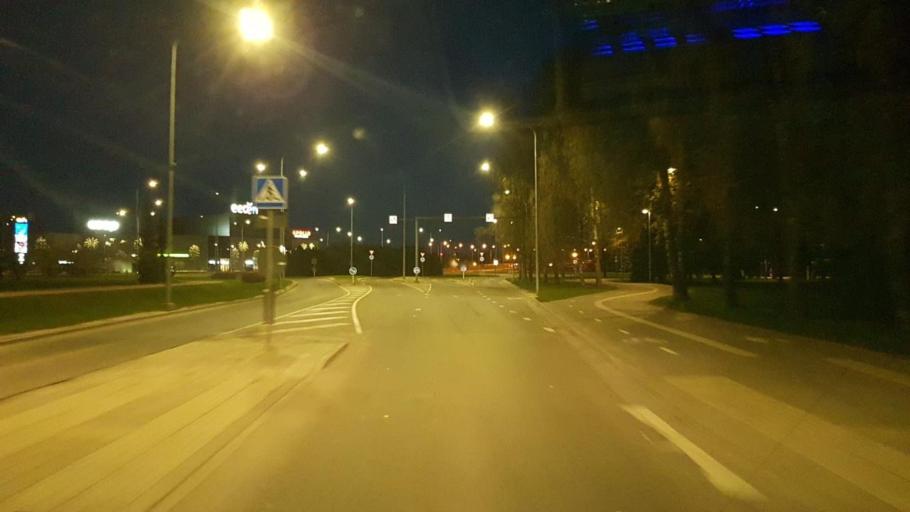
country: EE
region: Tartu
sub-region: Tartu linn
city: Tartu
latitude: 58.3760
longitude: 26.7499
